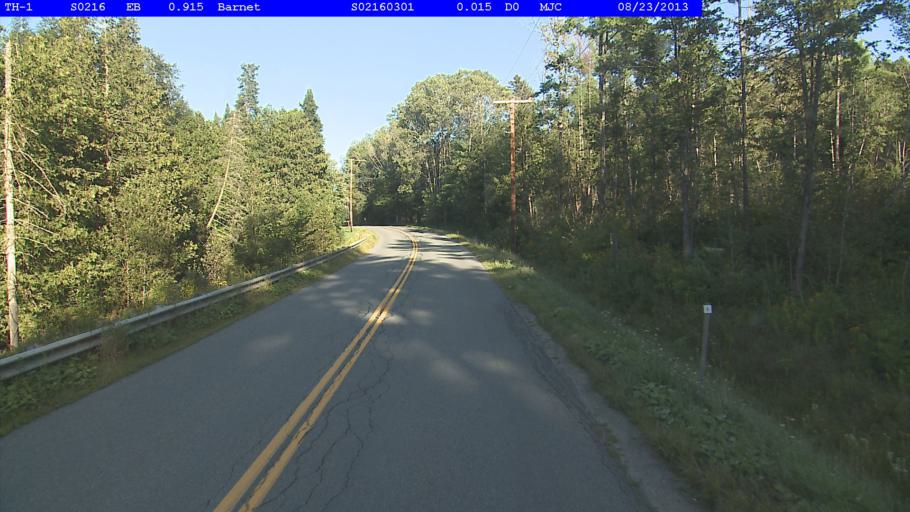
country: US
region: Vermont
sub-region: Caledonia County
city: Saint Johnsbury
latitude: 44.3084
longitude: -72.1507
